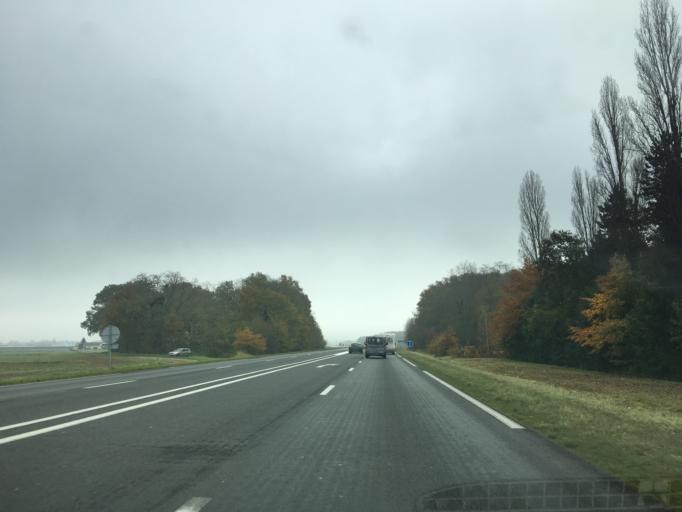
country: FR
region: Ile-de-France
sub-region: Departement de Seine-et-Marne
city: Barbizon
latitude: 48.4583
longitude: 2.5832
